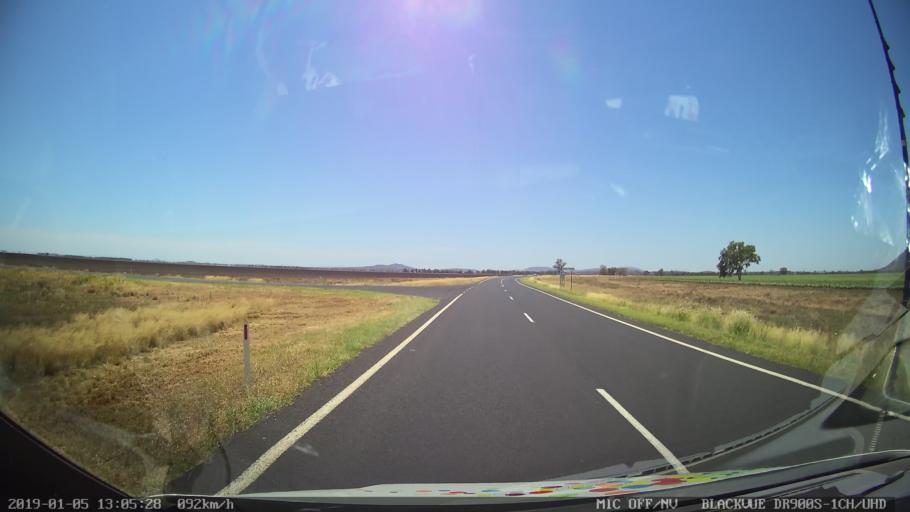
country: AU
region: New South Wales
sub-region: Gunnedah
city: Gunnedah
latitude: -31.0953
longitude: 149.8536
